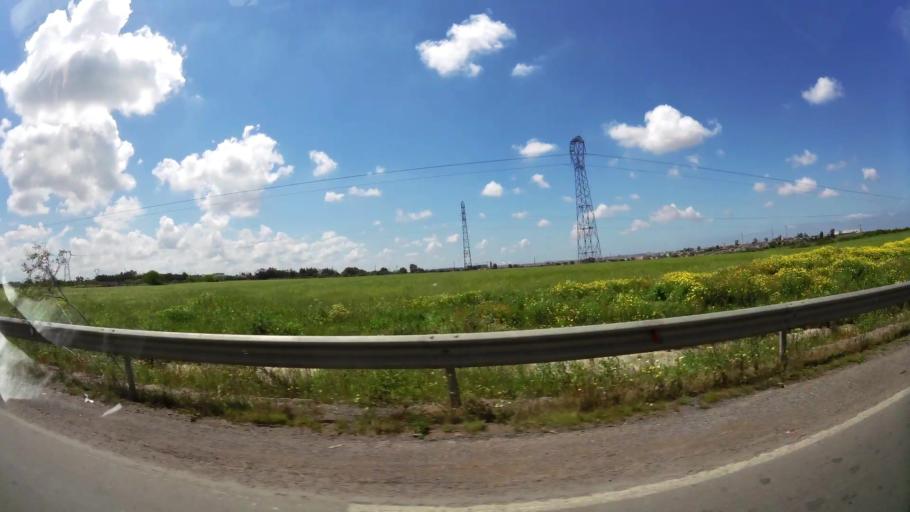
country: MA
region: Grand Casablanca
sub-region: Casablanca
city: Casablanca
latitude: 33.5150
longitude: -7.6141
